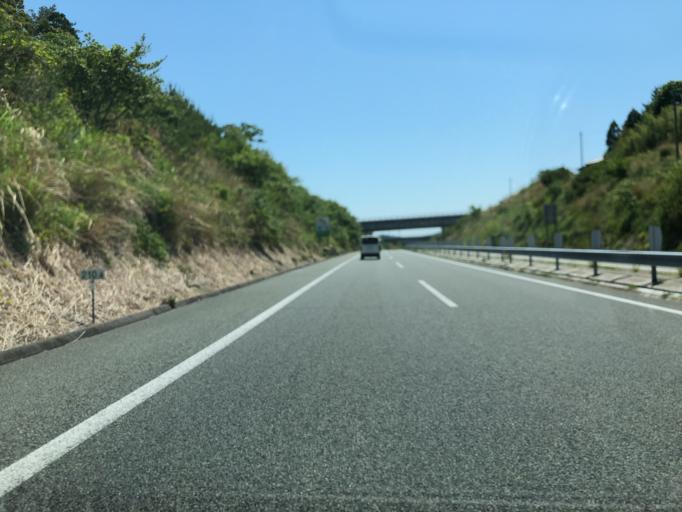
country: JP
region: Fukushima
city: Namie
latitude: 37.3087
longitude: 140.9920
